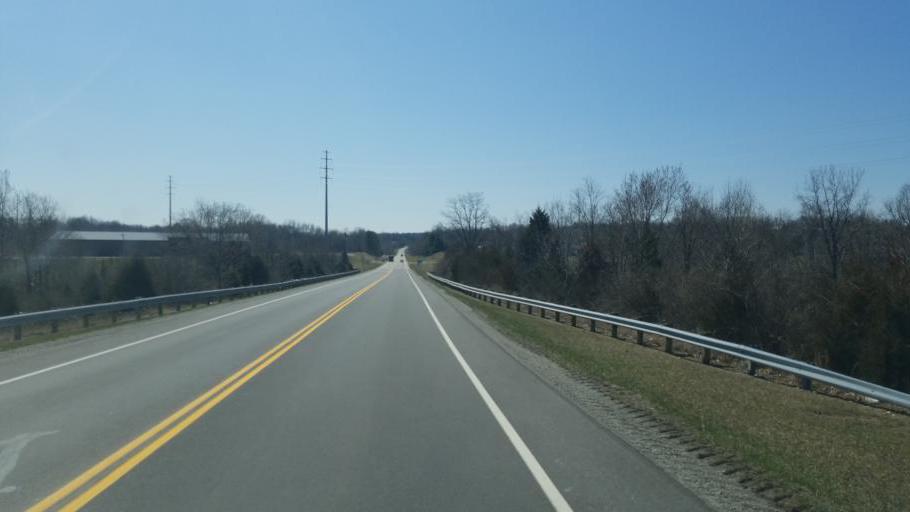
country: US
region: Ohio
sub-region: Highland County
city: Hillsboro
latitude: 39.1848
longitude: -83.6173
